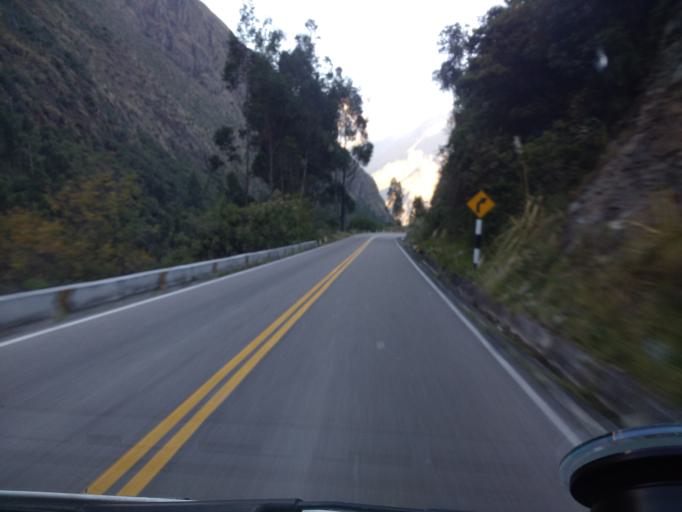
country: PE
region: Cusco
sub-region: Provincia de Urubamba
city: Ollantaytambo
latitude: -13.1984
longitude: -72.2946
